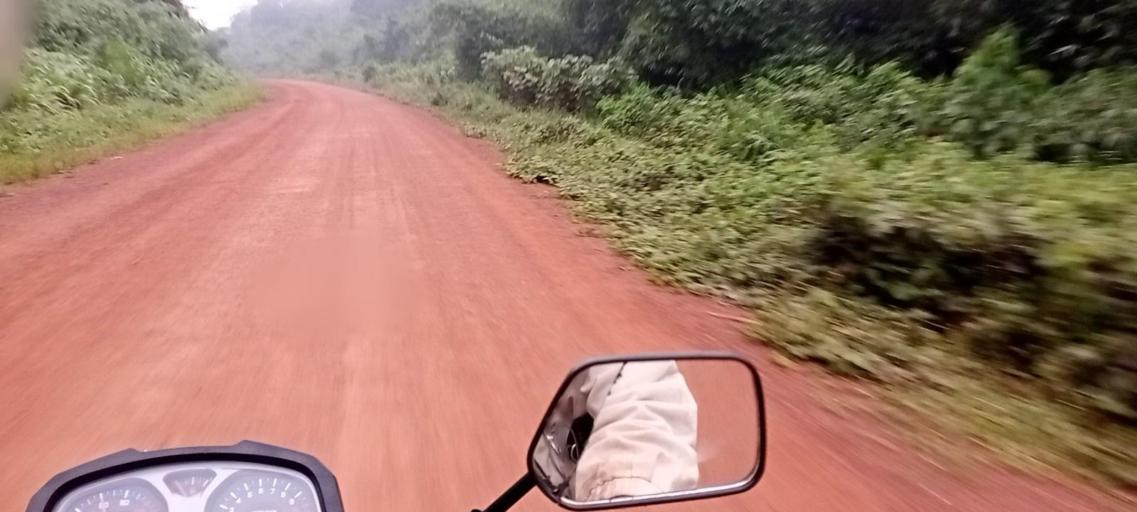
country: CD
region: Eastern Province
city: Kisangani
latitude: -0.0905
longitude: 25.6118
